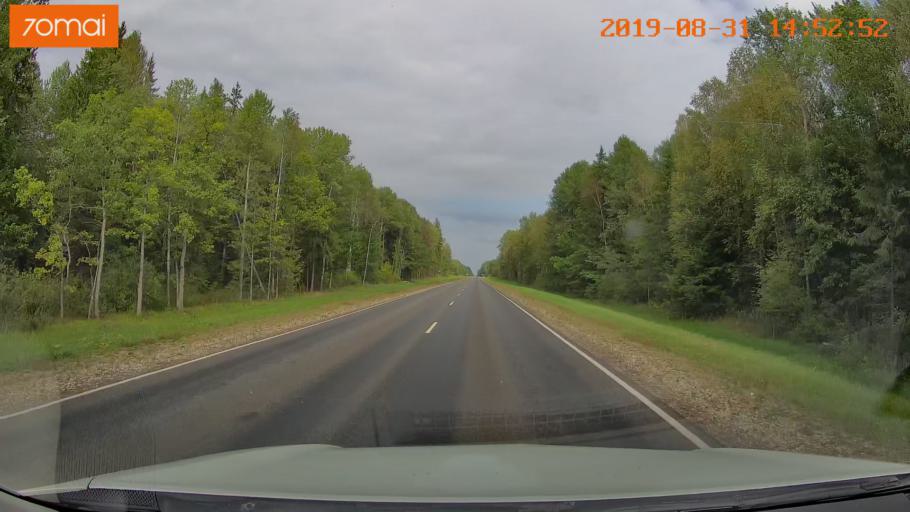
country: RU
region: Kaluga
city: Spas-Demensk
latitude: 54.2791
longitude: 33.8503
